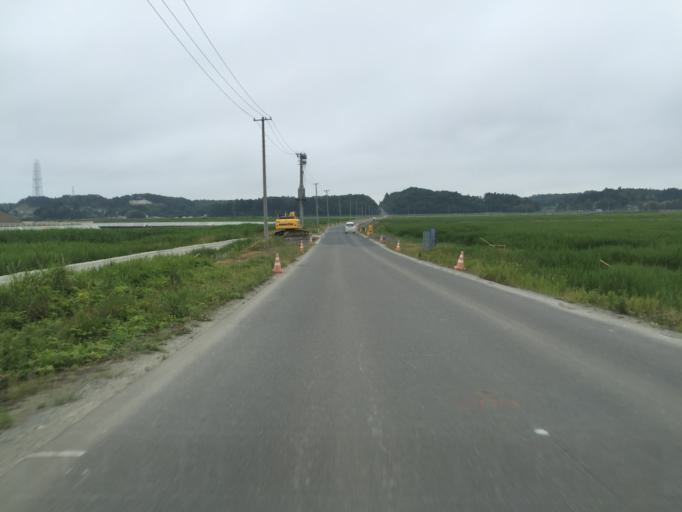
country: JP
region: Fukushima
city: Namie
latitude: 37.6856
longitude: 141.0050
